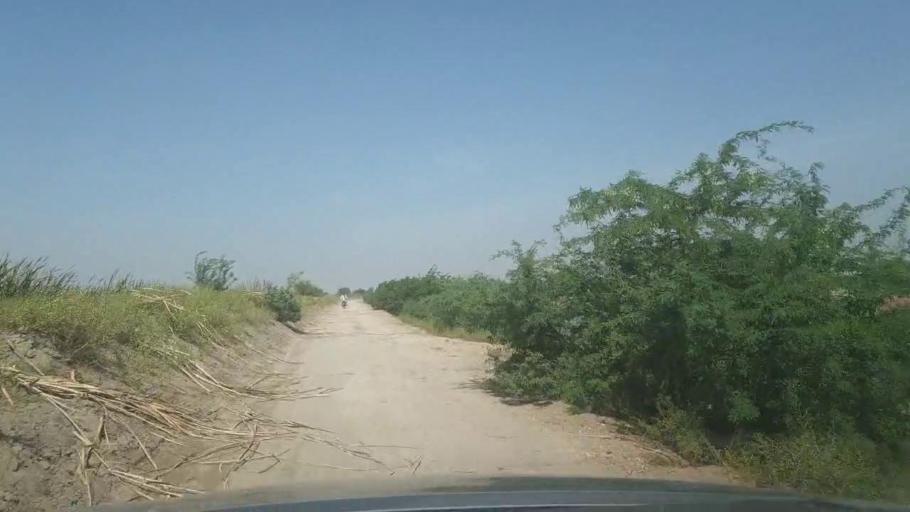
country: PK
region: Sindh
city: Khairpur
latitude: 27.3993
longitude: 69.0512
